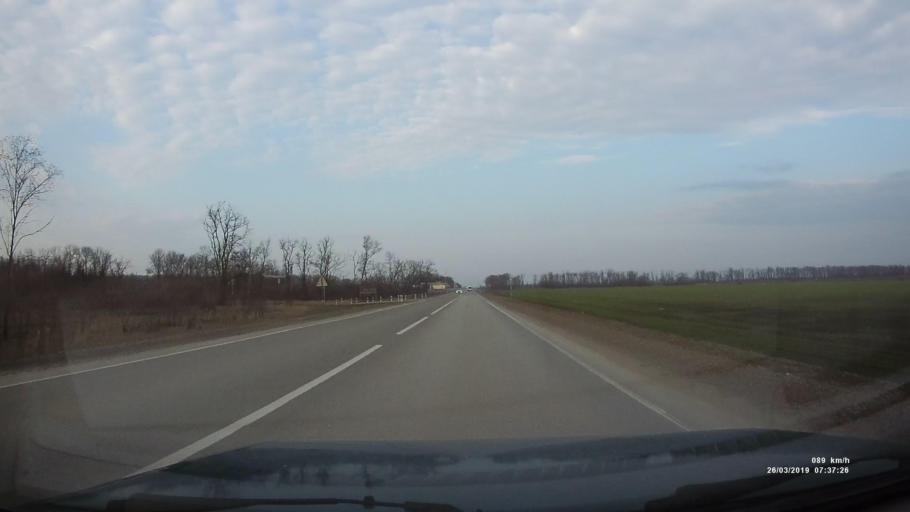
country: RU
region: Rostov
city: Novobessergenovka
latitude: 47.2024
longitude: 38.7014
